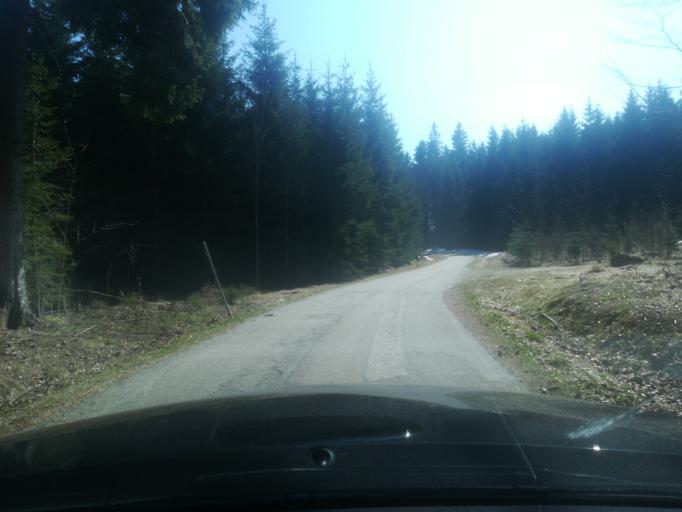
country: AT
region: Lower Austria
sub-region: Politischer Bezirk Zwettl
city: Langschlag
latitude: 48.5079
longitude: 14.8521
